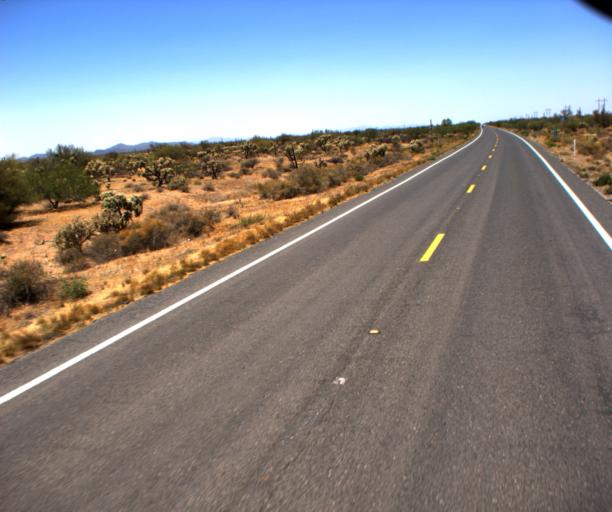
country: US
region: Arizona
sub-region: Pinal County
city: Florence
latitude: 32.7922
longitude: -111.1750
